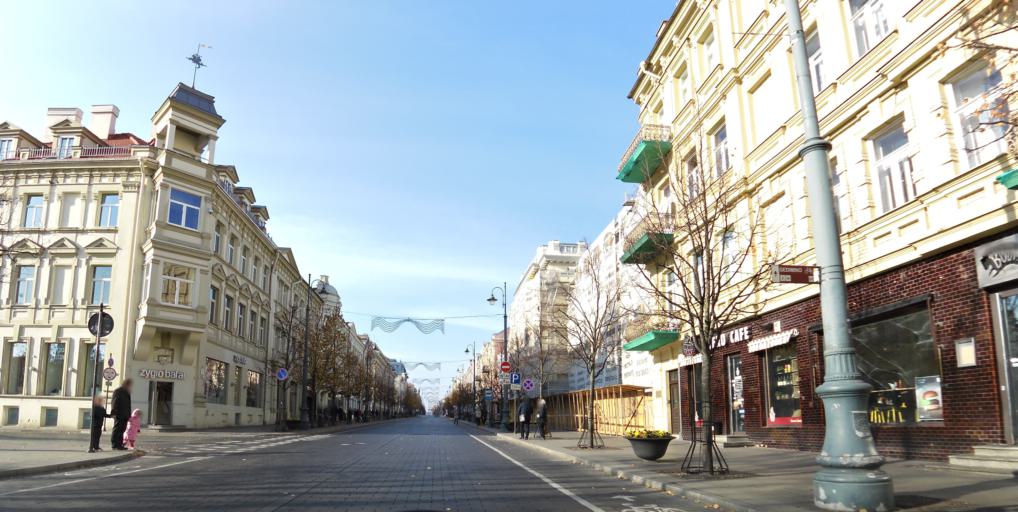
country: LT
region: Vilnius County
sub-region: Vilnius
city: Vilnius
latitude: 54.6861
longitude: 25.2857
